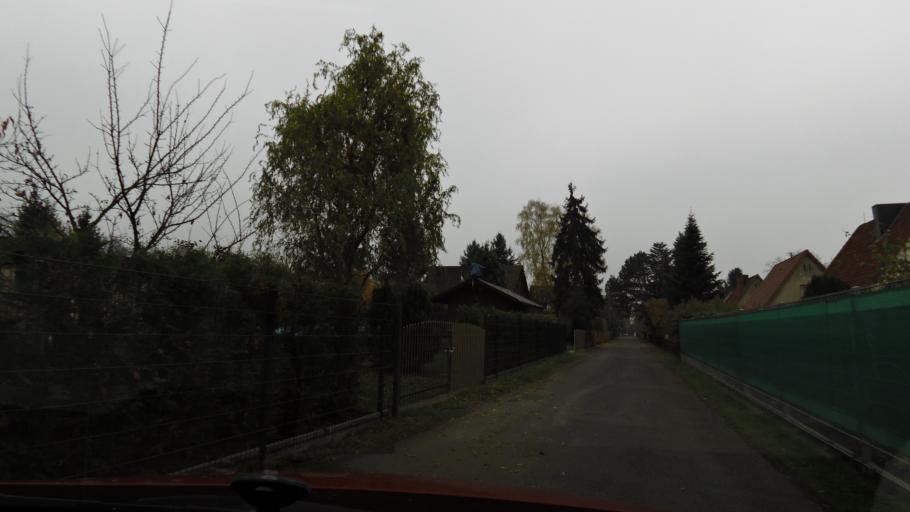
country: DE
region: Berlin
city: Lichtenrade
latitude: 52.3458
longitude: 13.4101
